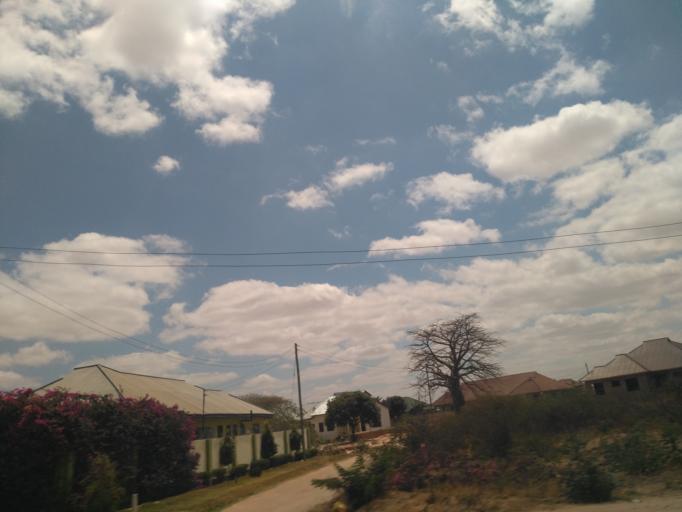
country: TZ
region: Dodoma
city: Kisasa
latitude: -6.1687
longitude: 35.8001
